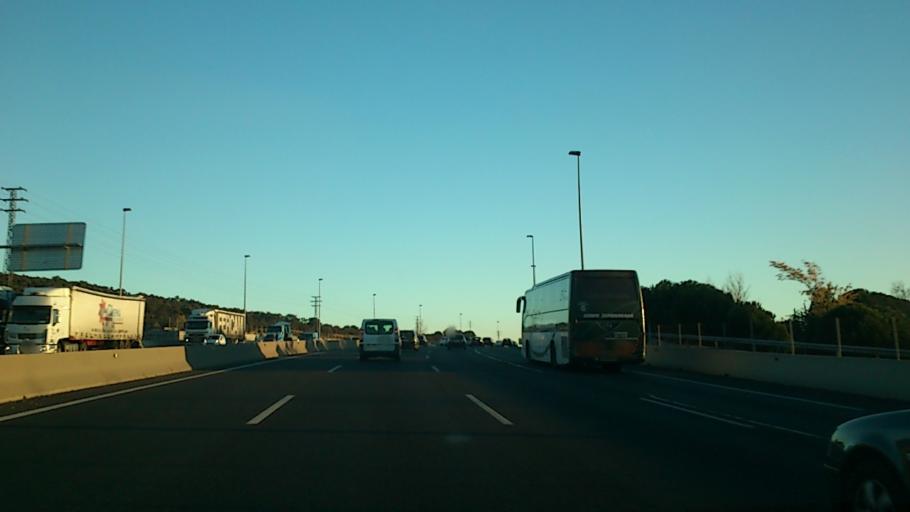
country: ES
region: Madrid
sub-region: Provincia de Madrid
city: Galapagar
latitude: 40.6034
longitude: -3.9654
